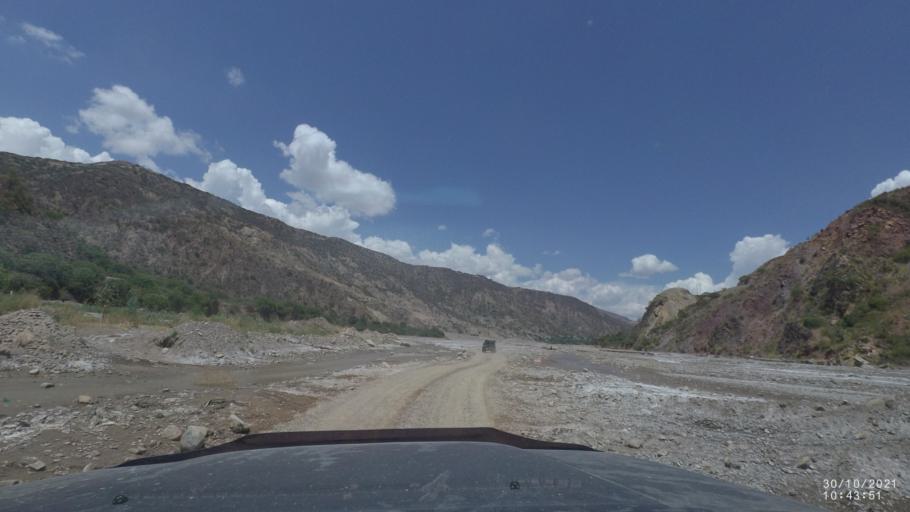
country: BO
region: Cochabamba
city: Sipe Sipe
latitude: -17.5607
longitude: -66.4476
